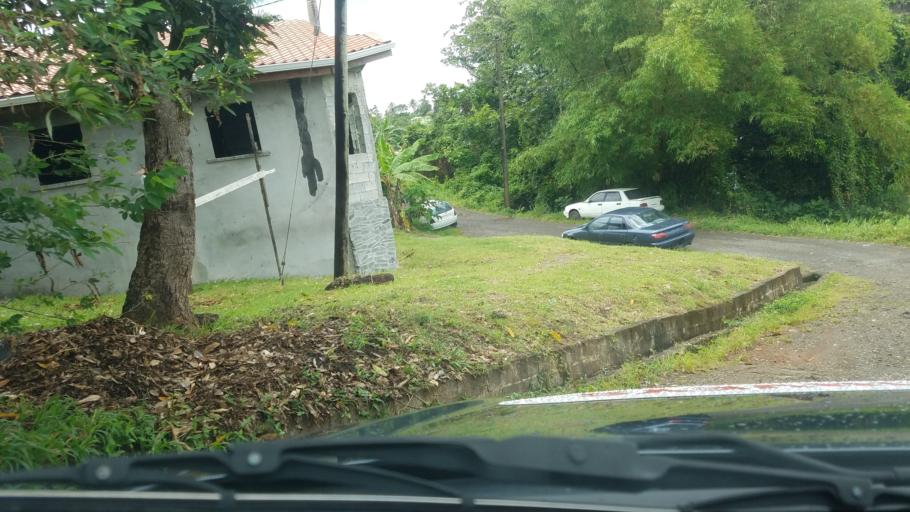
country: LC
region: Castries Quarter
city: Bisee
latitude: 14.0000
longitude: -60.9591
